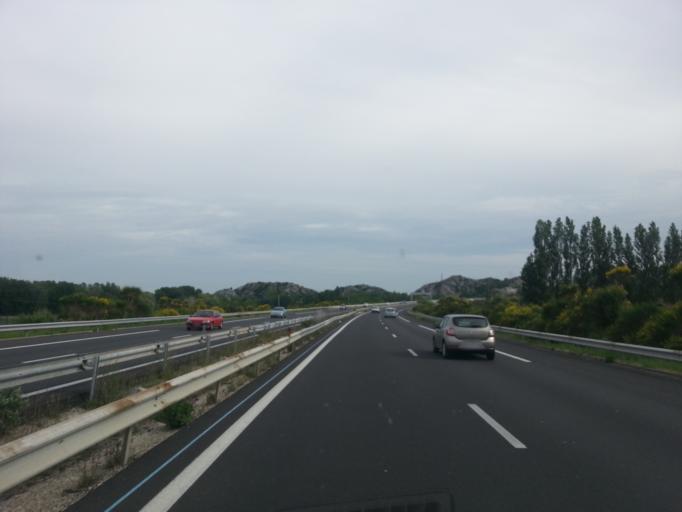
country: FR
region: Languedoc-Roussillon
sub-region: Departement du Gard
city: Roquemaure
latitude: 44.0606
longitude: 4.7666
